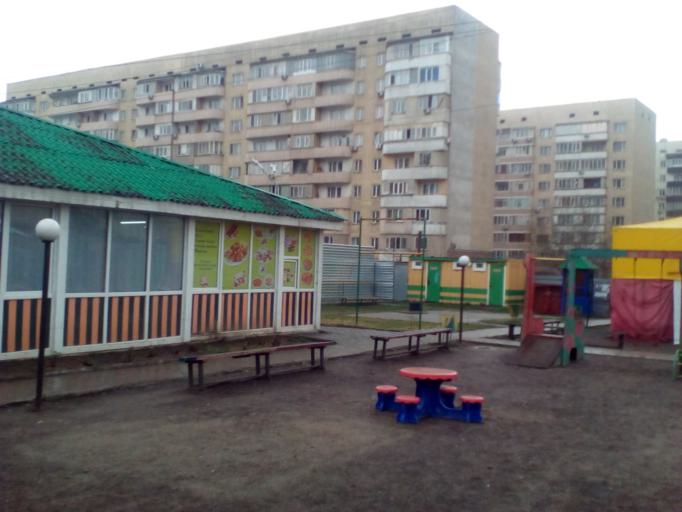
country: KZ
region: Almaty Qalasy
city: Almaty
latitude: 43.2405
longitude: 76.8255
